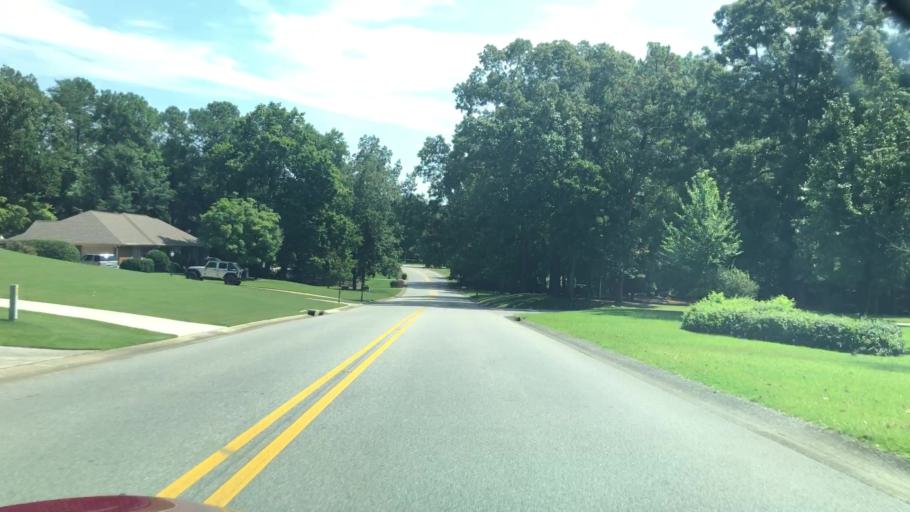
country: US
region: Alabama
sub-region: Shelby County
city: Meadowbrook
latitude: 33.4108
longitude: -86.6917
